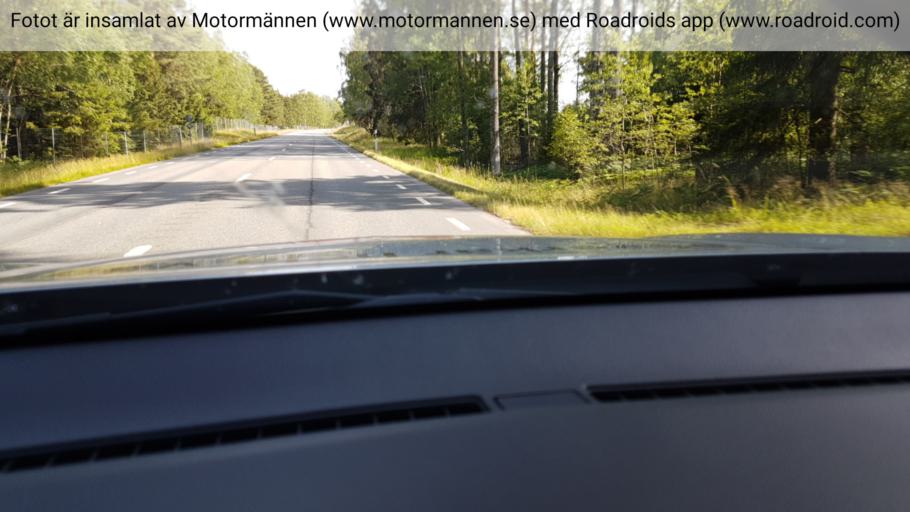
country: SE
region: Joenkoeping
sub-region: Eksjo Kommun
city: Eksjoe
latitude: 57.7130
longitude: 14.9441
